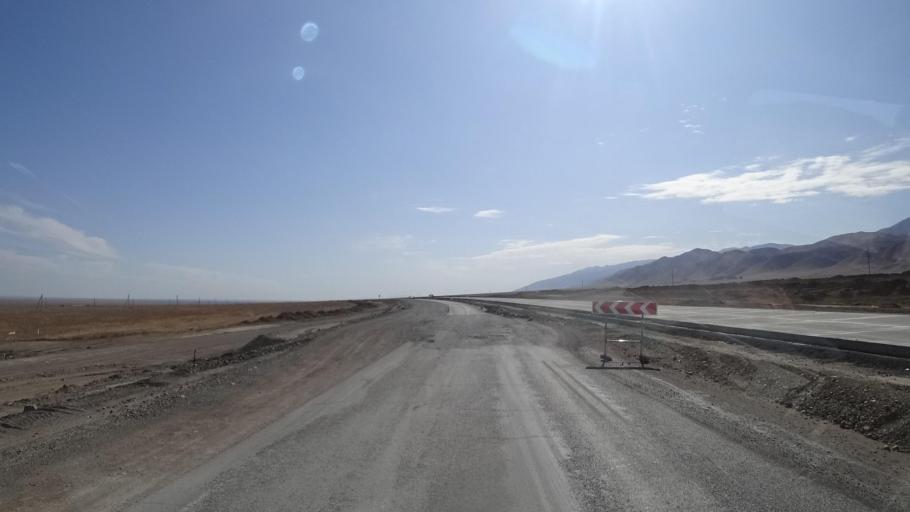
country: KG
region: Chuy
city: Ivanovka
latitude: 43.3874
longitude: 75.1503
